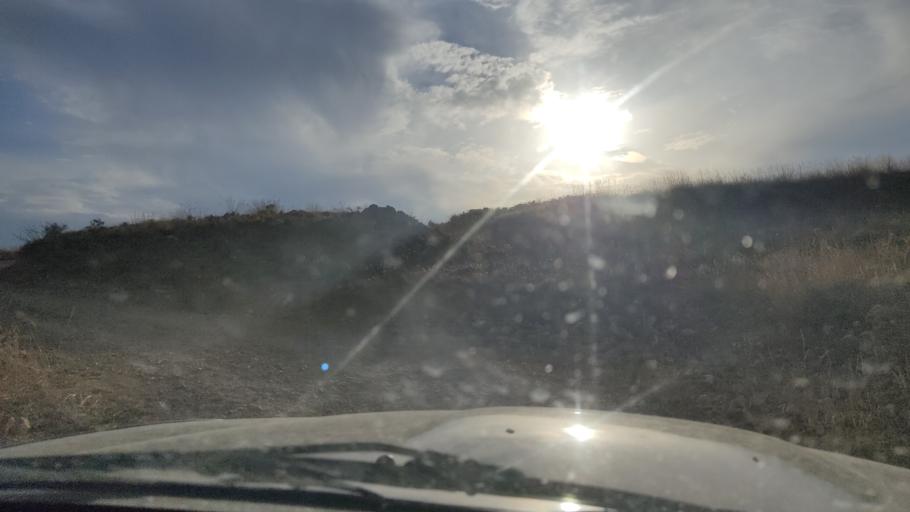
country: ES
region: Aragon
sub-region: Provincia de Teruel
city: Monforte de Moyuela
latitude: 41.0666
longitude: -0.9741
